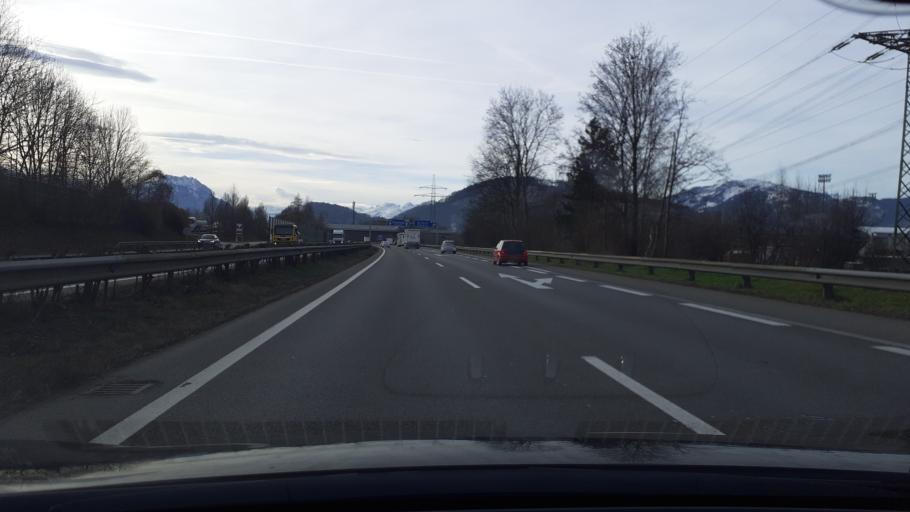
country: AT
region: Vorarlberg
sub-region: Politischer Bezirk Feldkirch
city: Altach
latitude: 47.3558
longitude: 9.6412
